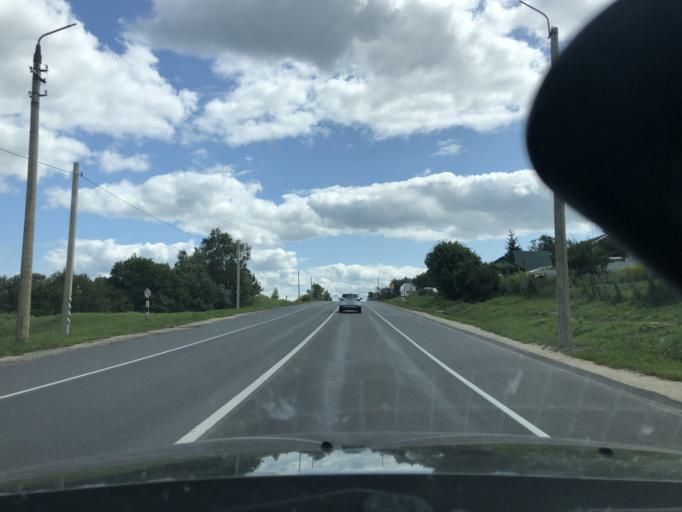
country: RU
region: Tula
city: Gorelki
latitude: 54.2972
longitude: 37.5770
